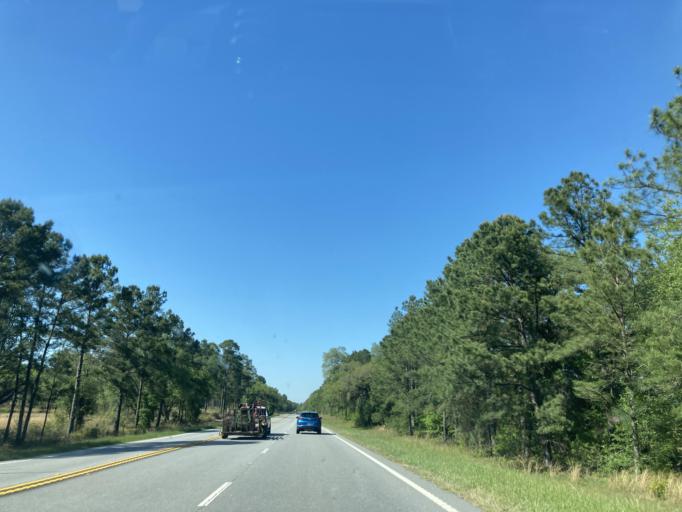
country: US
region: Georgia
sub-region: Baker County
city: Newton
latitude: 31.4112
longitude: -84.2763
